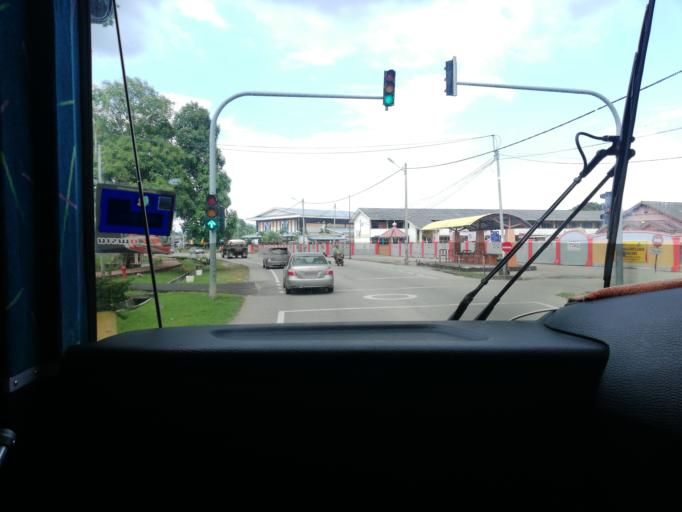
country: MY
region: Penang
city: Nibong Tebal
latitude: 5.2064
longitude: 100.6123
